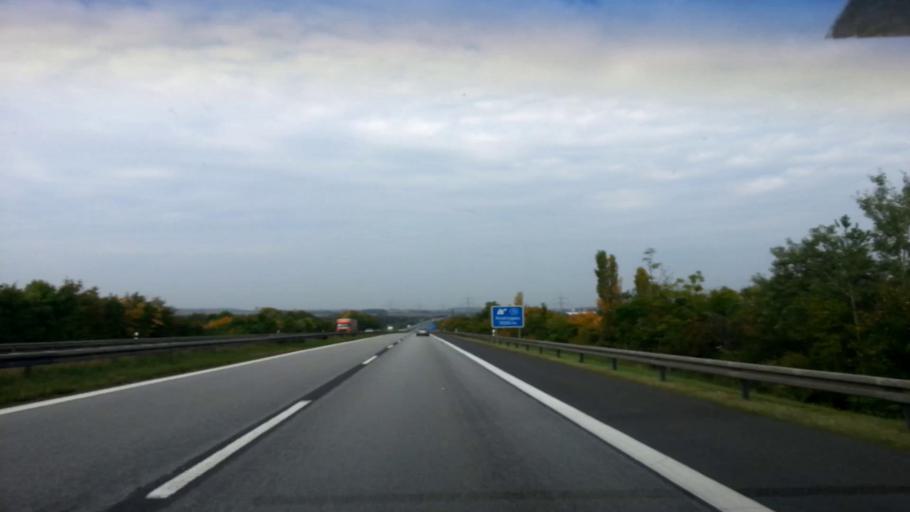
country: DE
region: Bavaria
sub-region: Regierungsbezirk Unterfranken
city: Sand
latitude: 49.9751
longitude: 10.5791
